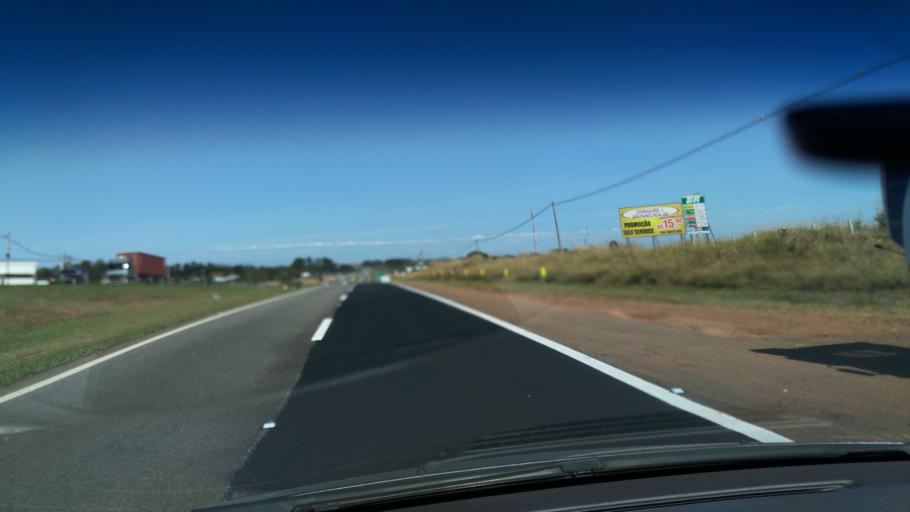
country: BR
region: Sao Paulo
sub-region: Santo Antonio De Posse
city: Santo Antonio de Posse
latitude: -22.6035
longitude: -47.0077
